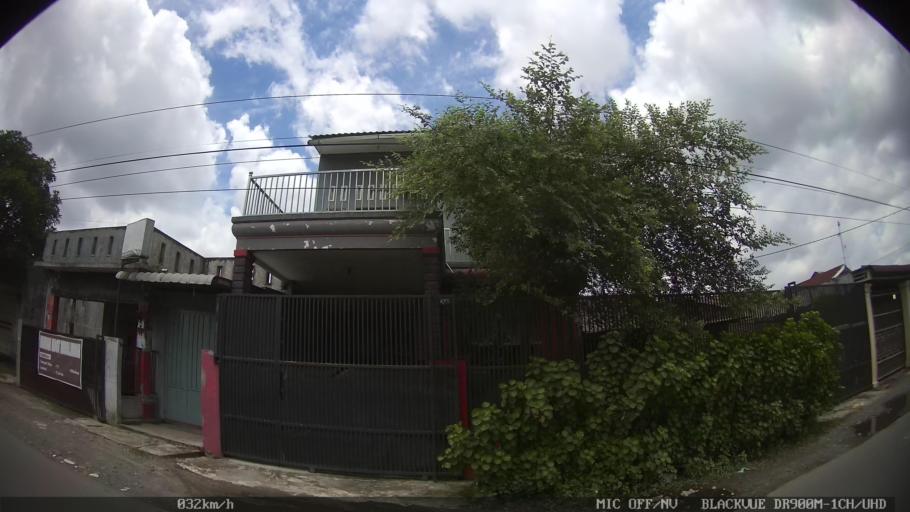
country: ID
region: North Sumatra
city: Medan
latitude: 3.6042
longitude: 98.7287
